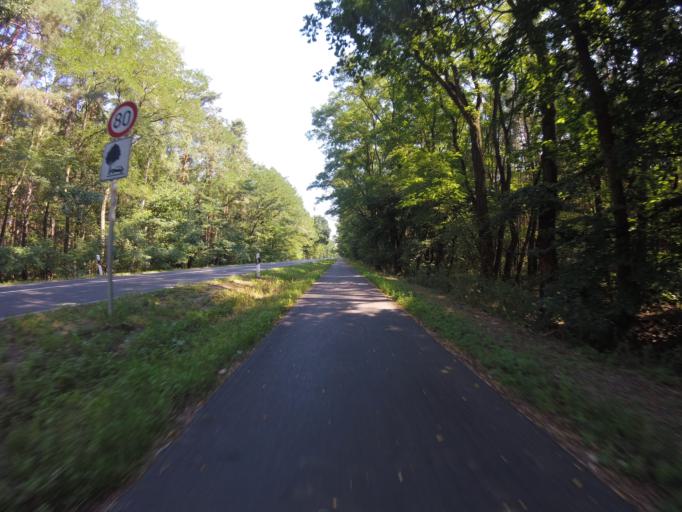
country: DE
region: Brandenburg
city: Mullrose
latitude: 52.2607
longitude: 14.4296
